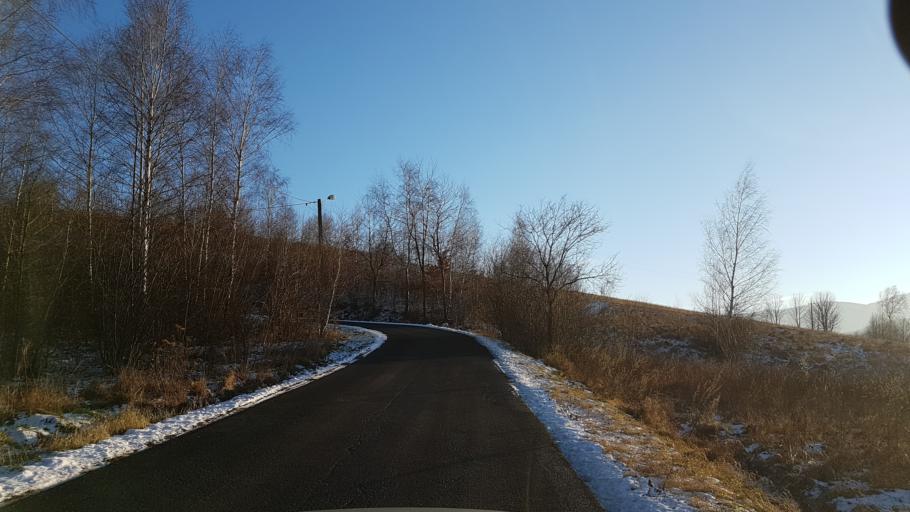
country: PL
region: Lesser Poland Voivodeship
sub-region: Powiat nowosadecki
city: Rytro
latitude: 49.5152
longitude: 20.6637
